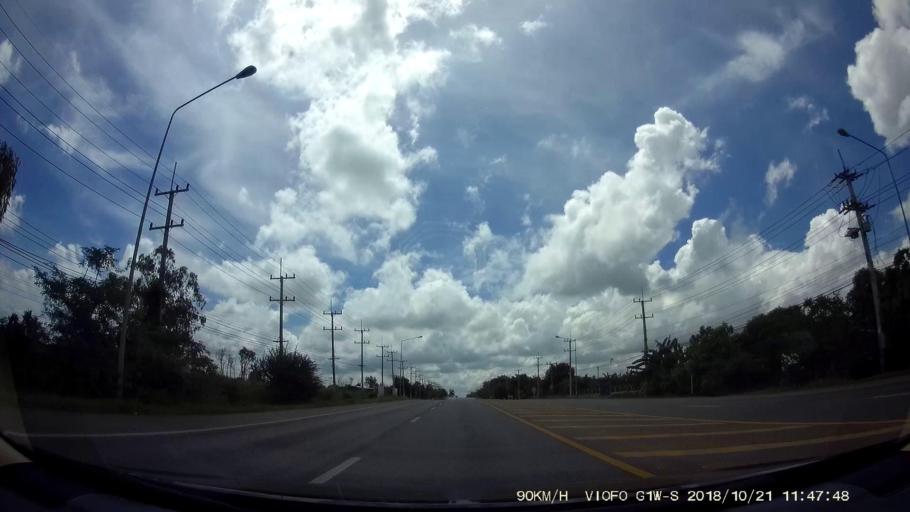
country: TH
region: Chaiyaphum
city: Noen Sa-nga
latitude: 15.6565
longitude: 101.9520
